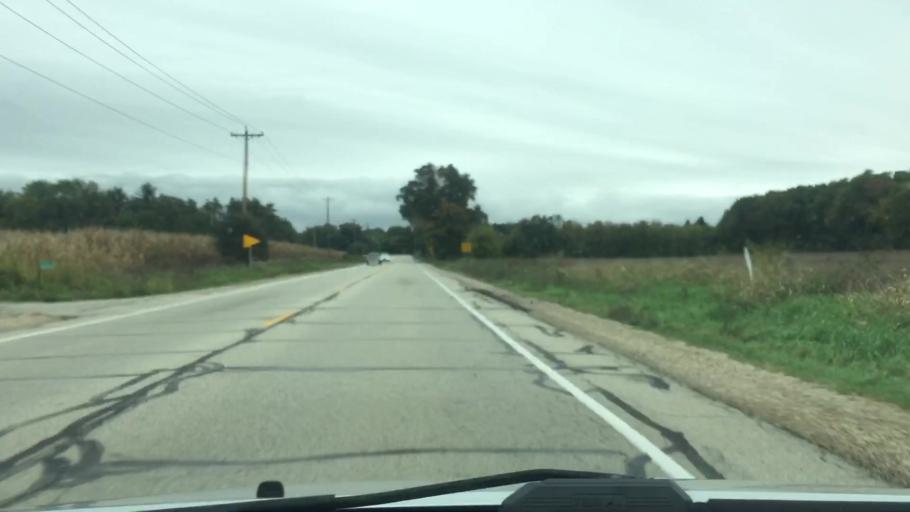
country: US
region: Wisconsin
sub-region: Jefferson County
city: Palmyra
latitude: 42.7929
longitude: -88.5630
